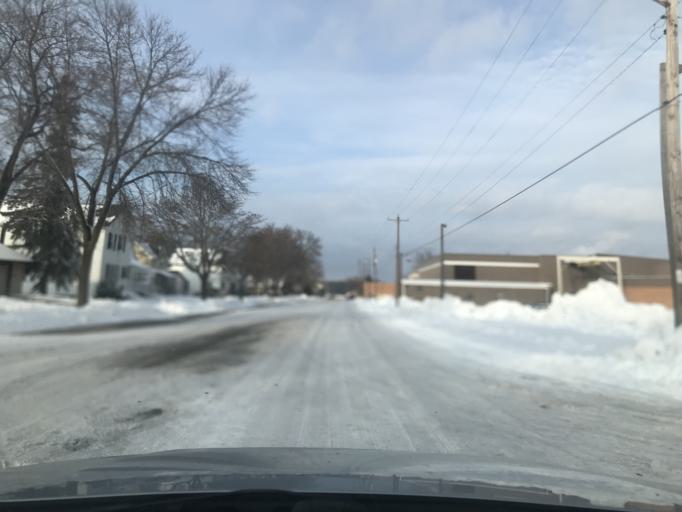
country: US
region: Wisconsin
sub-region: Marinette County
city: Peshtigo
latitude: 45.0511
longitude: -87.7491
